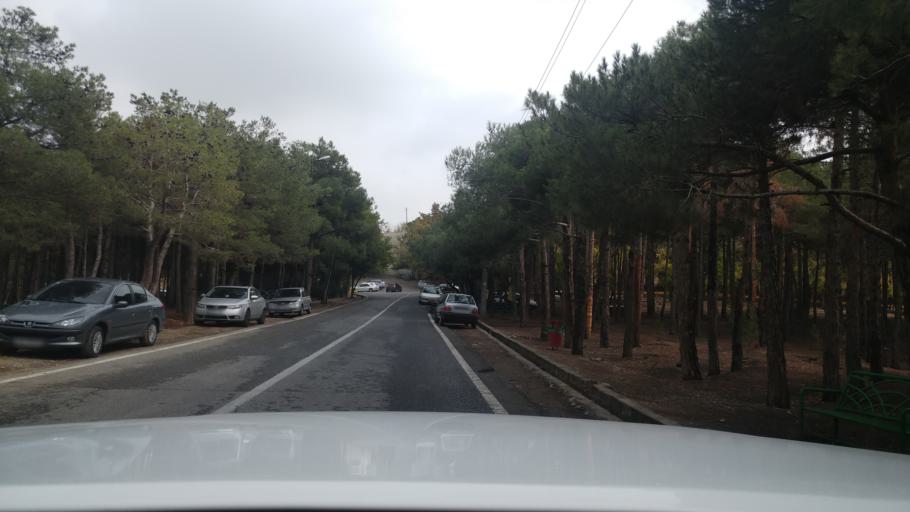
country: IR
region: Tehran
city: Shahr-e Qods
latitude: 35.7267
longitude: 51.2222
